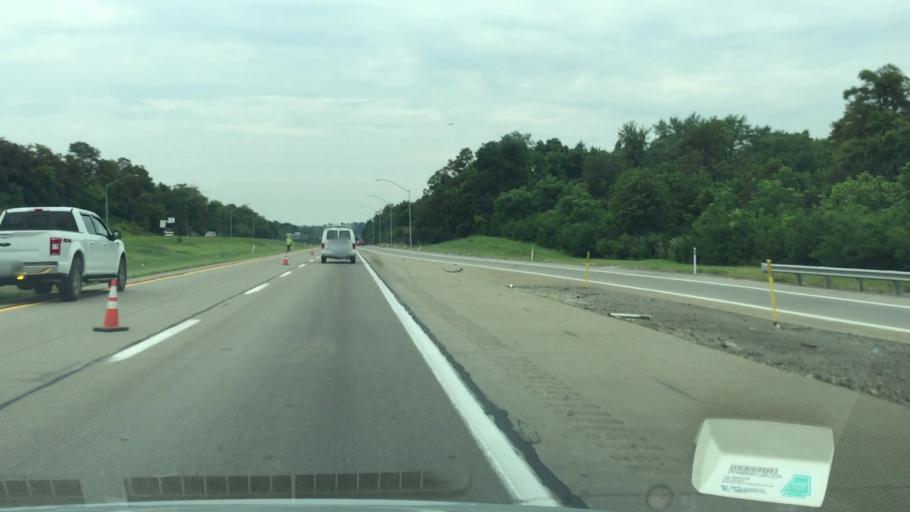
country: US
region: Pennsylvania
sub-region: Allegheny County
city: Ingram
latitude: 40.4522
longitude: -80.1110
